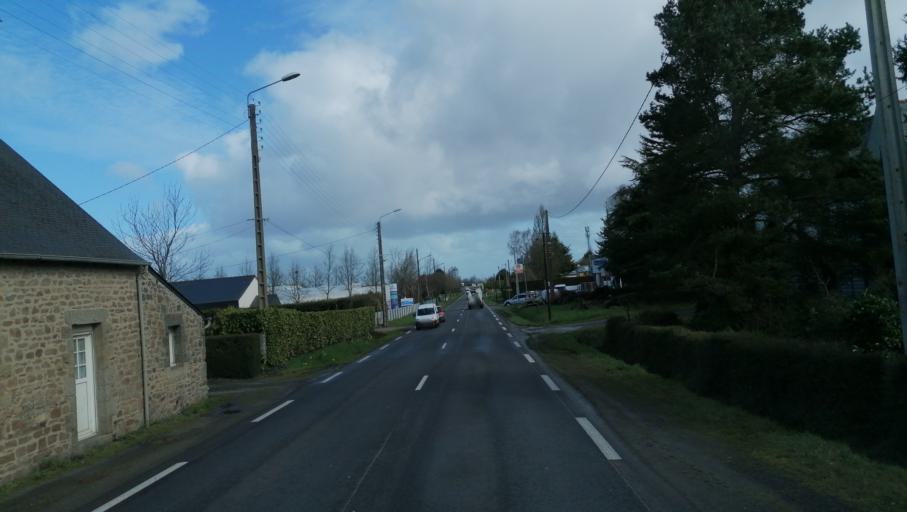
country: FR
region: Brittany
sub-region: Departement des Cotes-d'Armor
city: Ploufragan
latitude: 48.4764
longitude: -2.7979
